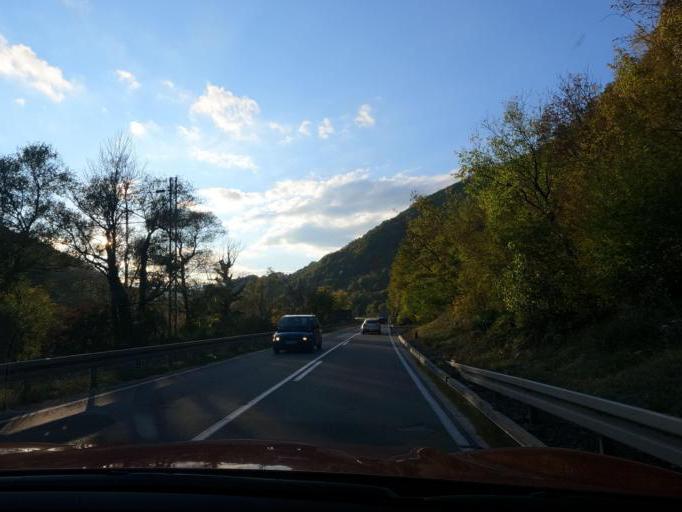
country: RS
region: Central Serbia
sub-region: Moravicki Okrug
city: Lucani
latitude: 43.8984
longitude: 20.1671
